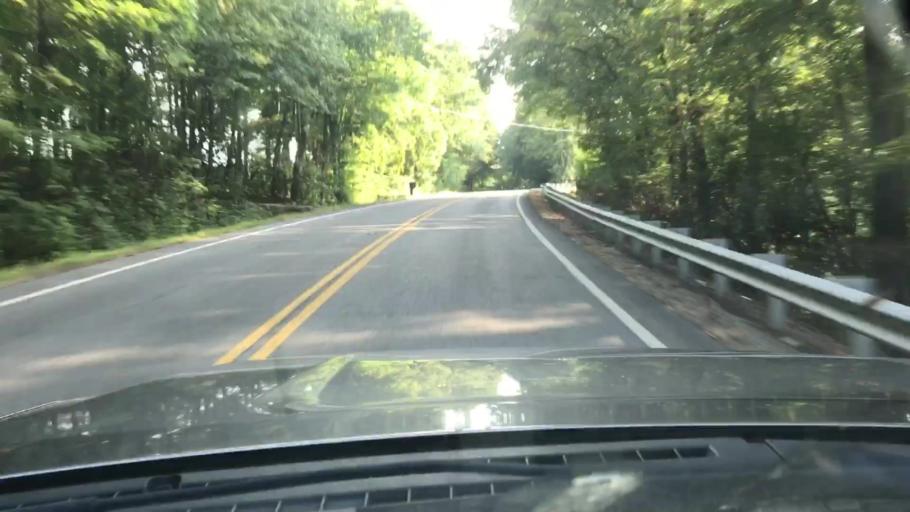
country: US
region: Tennessee
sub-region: Sumner County
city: Gallatin
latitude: 36.4868
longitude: -86.4351
